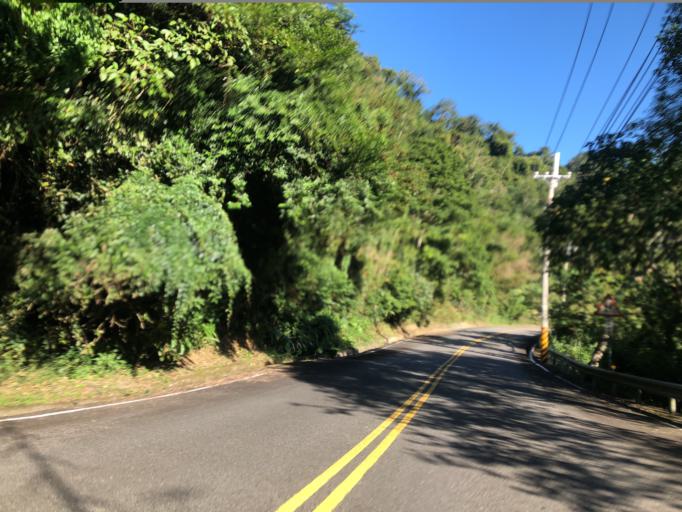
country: TW
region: Taiwan
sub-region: Miaoli
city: Miaoli
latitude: 24.5786
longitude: 120.9343
